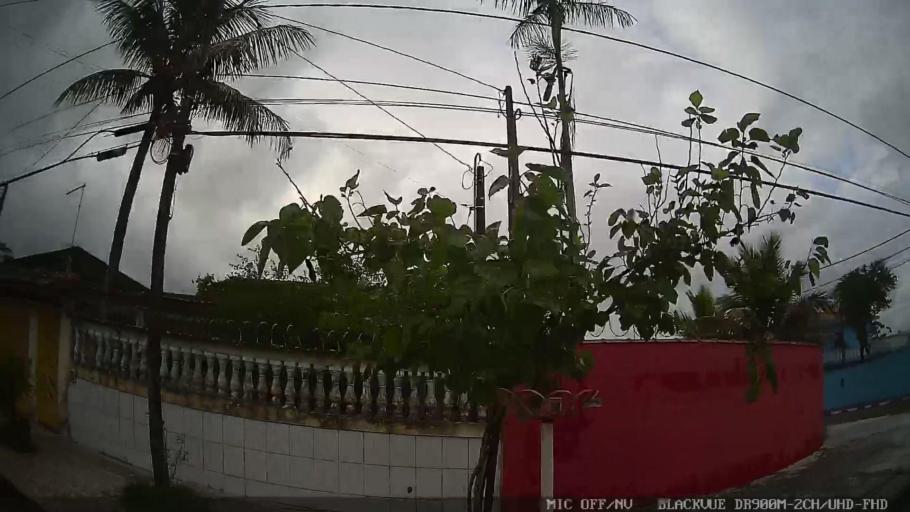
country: BR
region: Sao Paulo
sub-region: Itanhaem
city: Itanhaem
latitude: -24.2175
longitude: -46.8602
